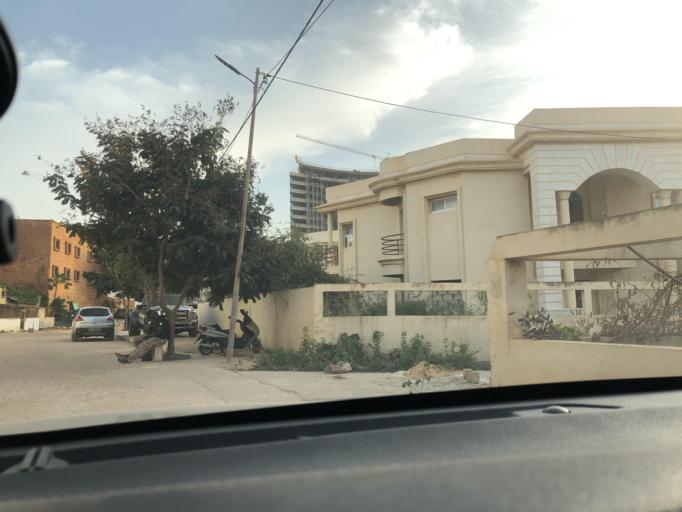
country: SN
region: Dakar
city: Mermoz Boabab
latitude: 14.7293
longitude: -17.5021
